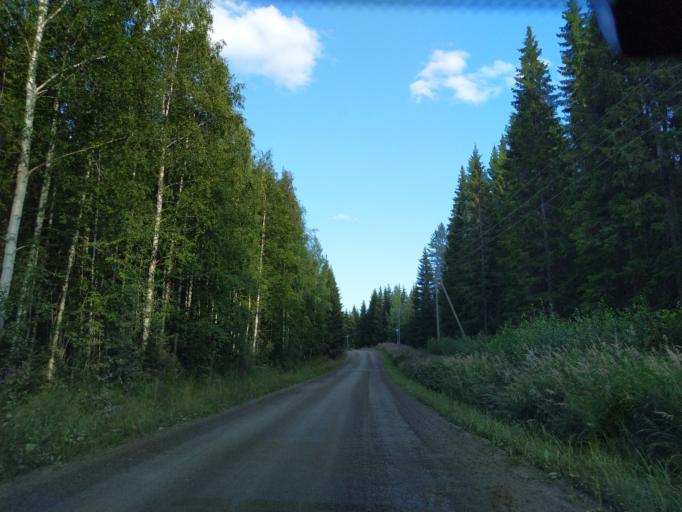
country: FI
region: Central Finland
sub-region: Jaemsae
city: Kuhmoinen
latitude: 61.6952
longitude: 24.9332
